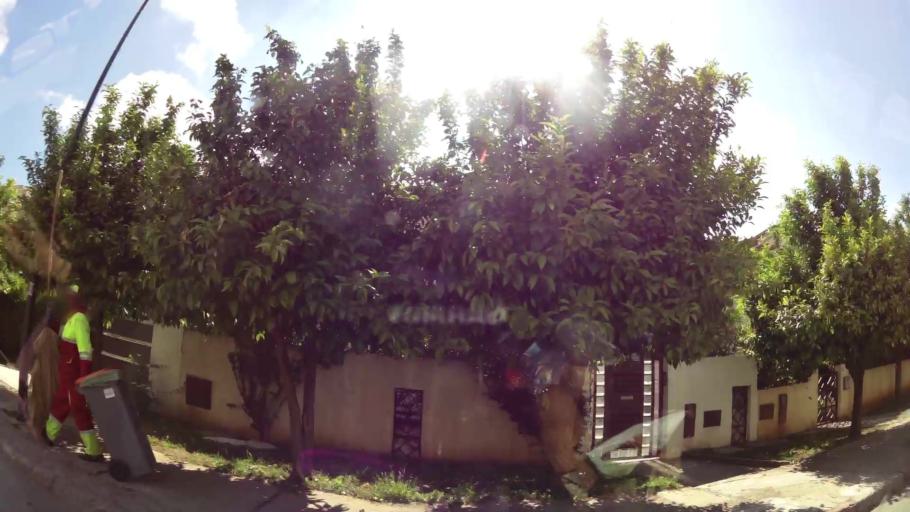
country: MA
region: Fes-Boulemane
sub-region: Fes
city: Fes
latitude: 34.0341
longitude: -5.0226
